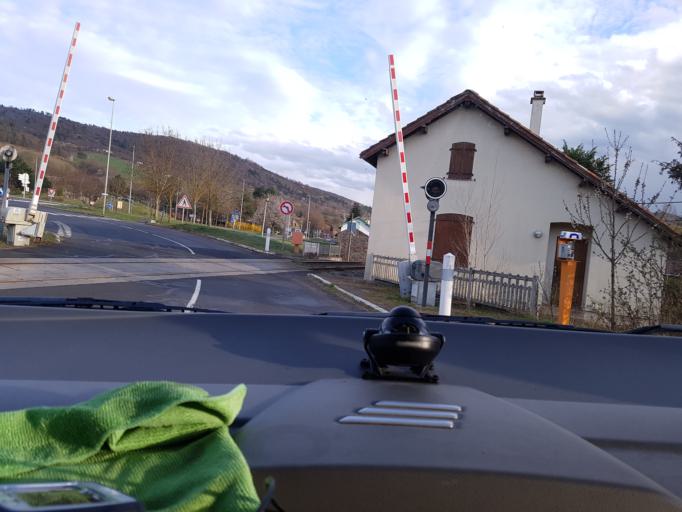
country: FR
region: Auvergne
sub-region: Departement du Cantal
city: Massiac
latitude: 45.2630
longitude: 3.1970
